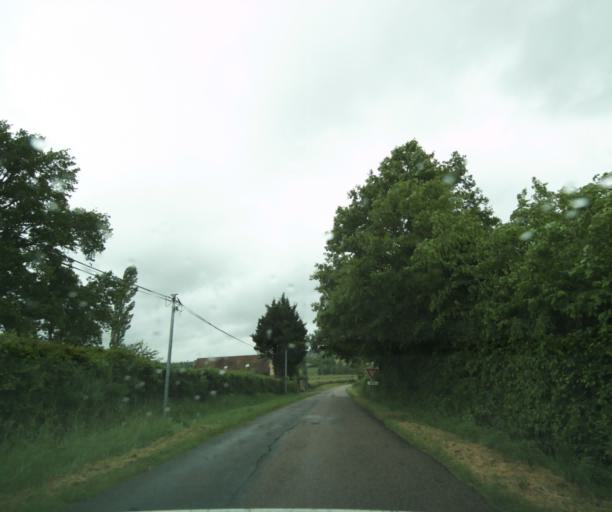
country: FR
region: Bourgogne
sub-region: Departement de Saone-et-Loire
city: Charolles
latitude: 46.4650
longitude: 4.4375
